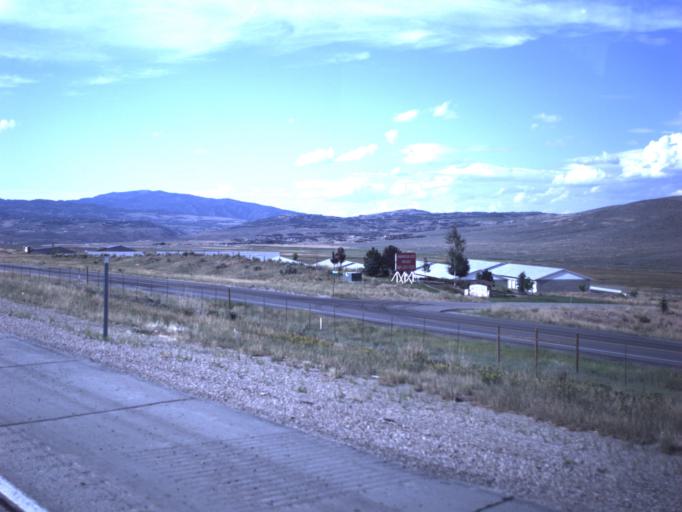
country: US
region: Utah
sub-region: Summit County
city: Park City
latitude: 40.6937
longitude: -111.4694
